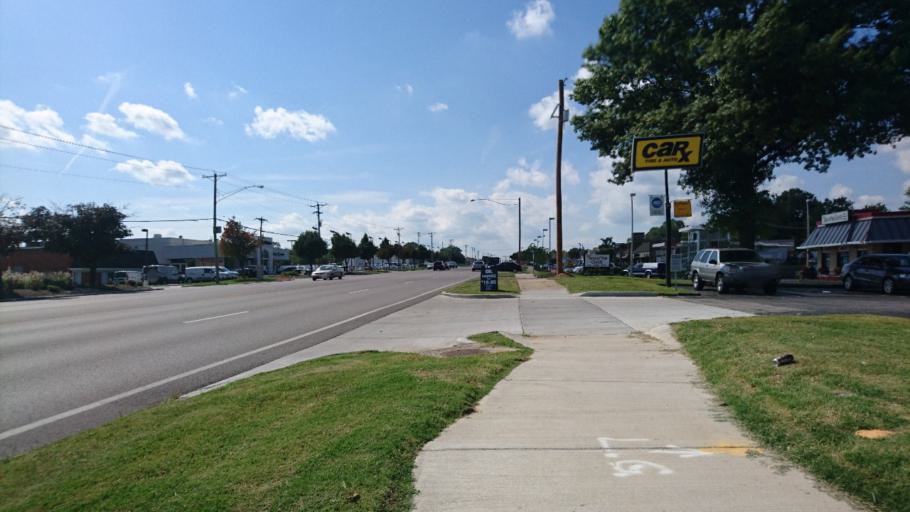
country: US
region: Missouri
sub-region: Saint Louis County
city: Ellisville
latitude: 38.5929
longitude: -90.5671
